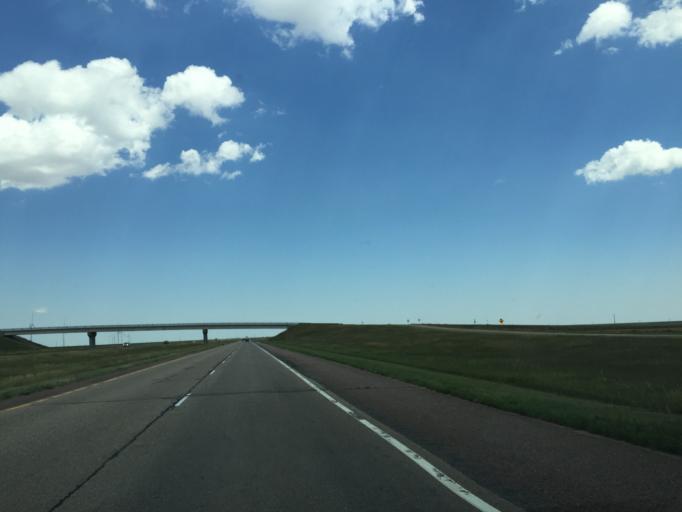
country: US
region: Colorado
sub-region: Lincoln County
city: Hugo
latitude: 39.2779
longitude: -103.4384
